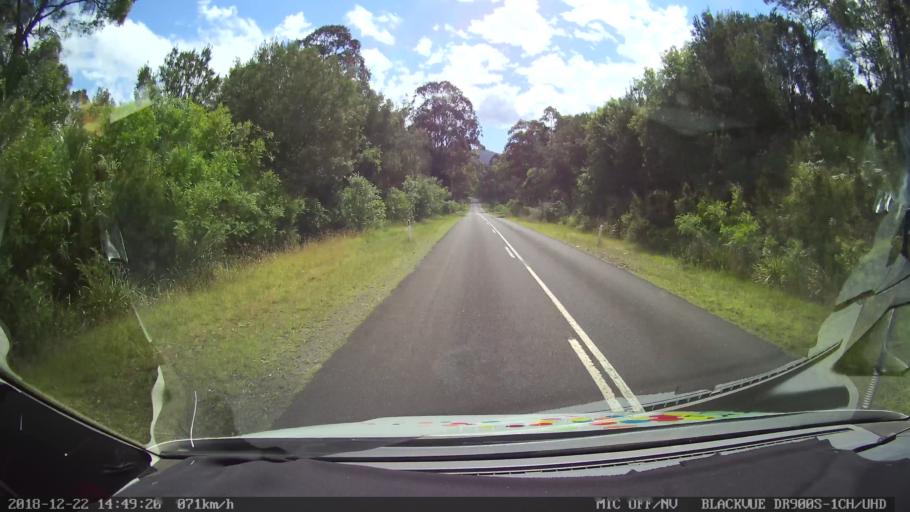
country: AU
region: New South Wales
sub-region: Bellingen
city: Dorrigo
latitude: -30.1884
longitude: 152.5489
